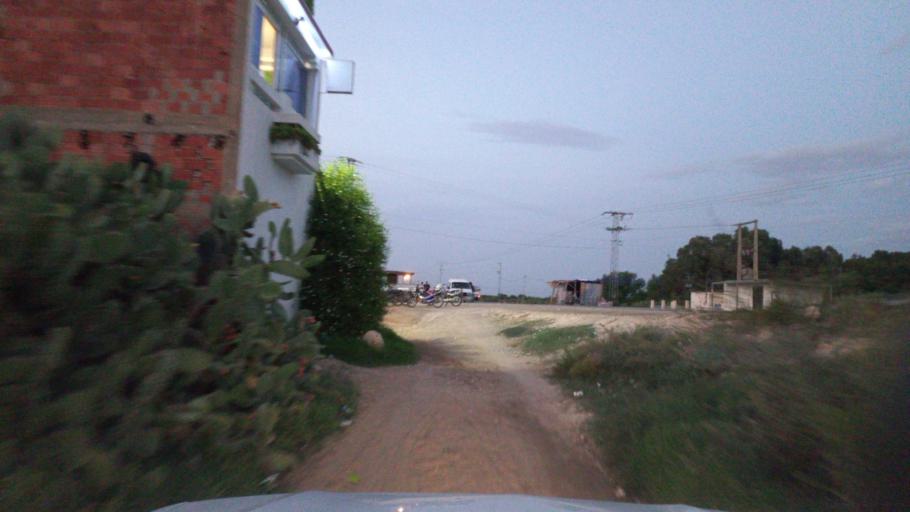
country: TN
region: Al Qasrayn
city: Sbiba
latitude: 35.4160
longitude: 9.1252
